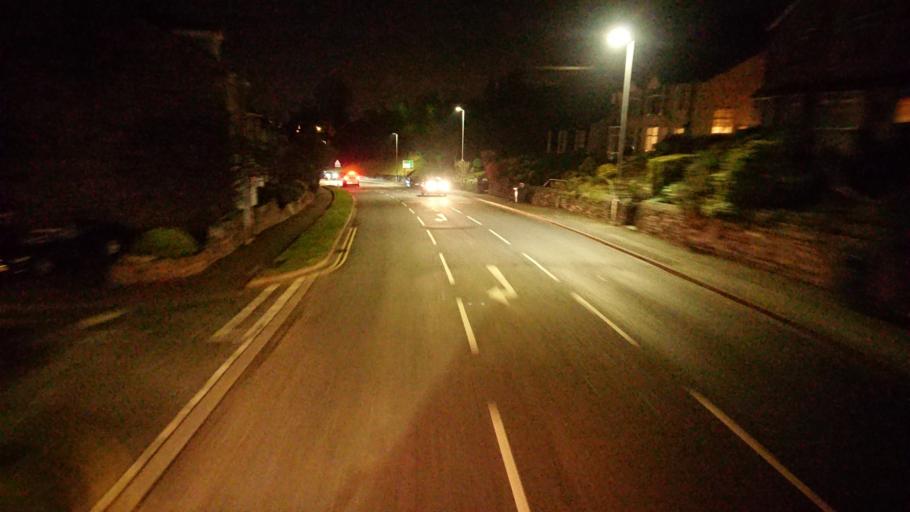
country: GB
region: England
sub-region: Cumbria
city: Kendal
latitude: 54.3340
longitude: -2.7557
